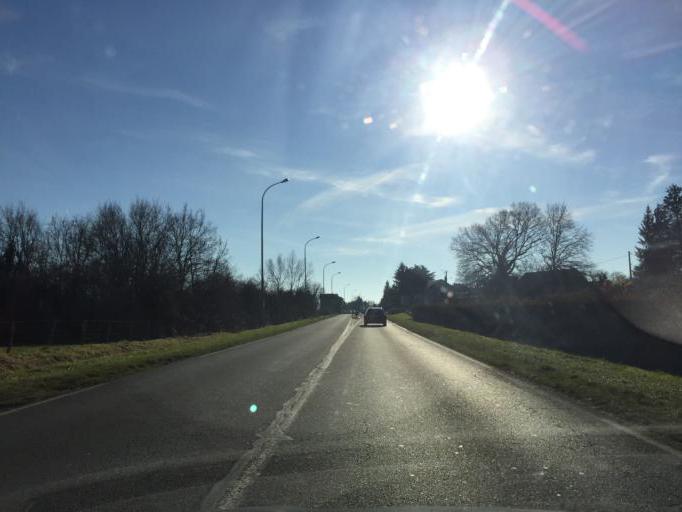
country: FR
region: Auvergne
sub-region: Departement de l'Allier
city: Bellerive-sur-Allier
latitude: 46.1494
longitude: 3.3942
